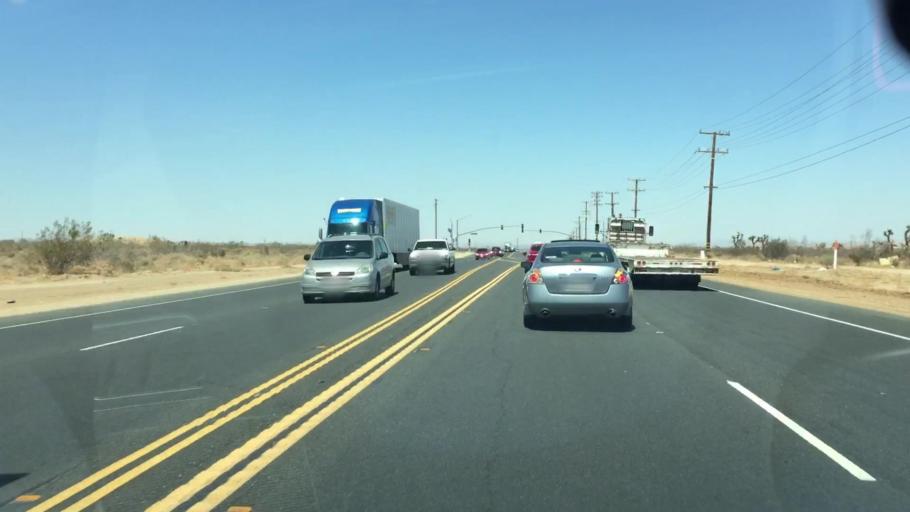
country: US
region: California
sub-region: San Bernardino County
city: Mountain View Acres
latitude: 34.4534
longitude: -117.3996
